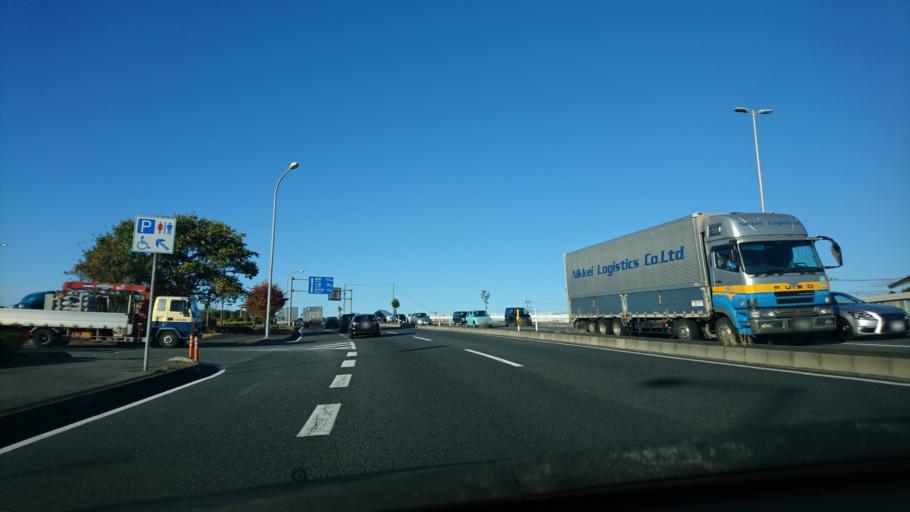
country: JP
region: Gunma
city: Annaka
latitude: 36.3357
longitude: 138.9392
